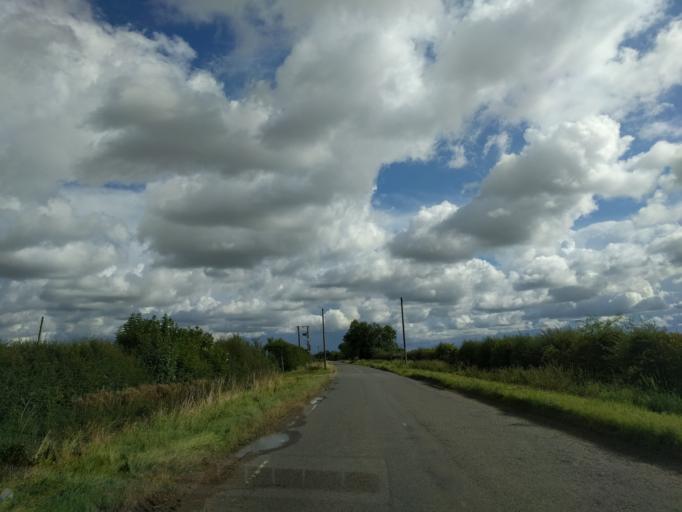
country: GB
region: England
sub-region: Lincolnshire
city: Long Bennington
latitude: 53.0349
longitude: -0.7545
